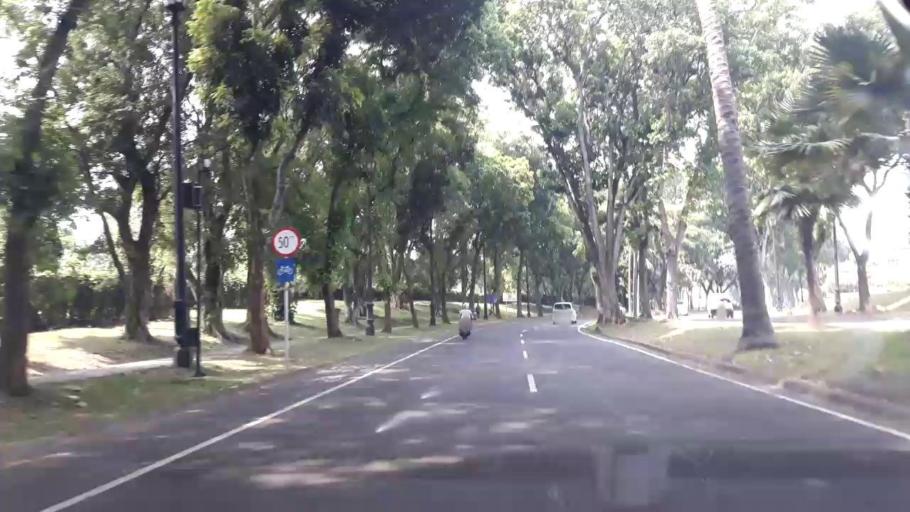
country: ID
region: Banten
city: Curug
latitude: -6.2368
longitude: 106.6082
